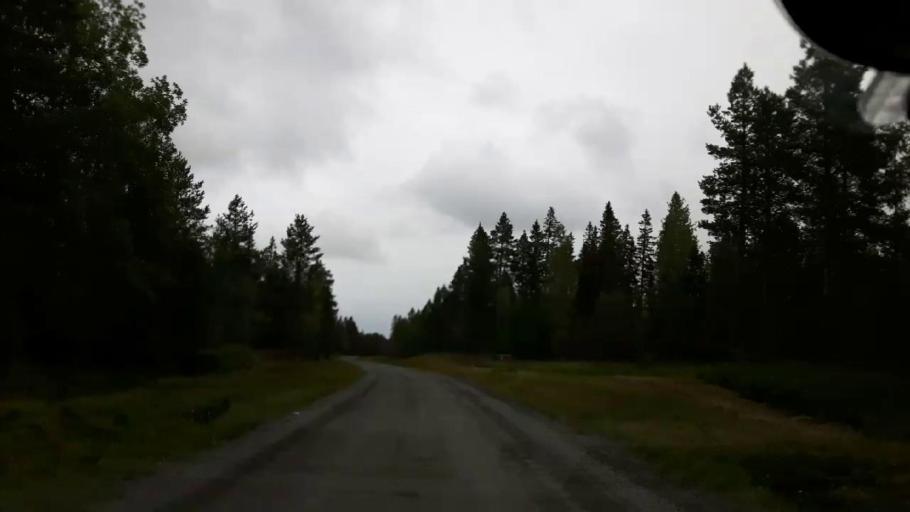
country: SE
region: Jaemtland
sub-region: OEstersunds Kommun
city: Ostersund
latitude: 63.0795
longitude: 14.5551
